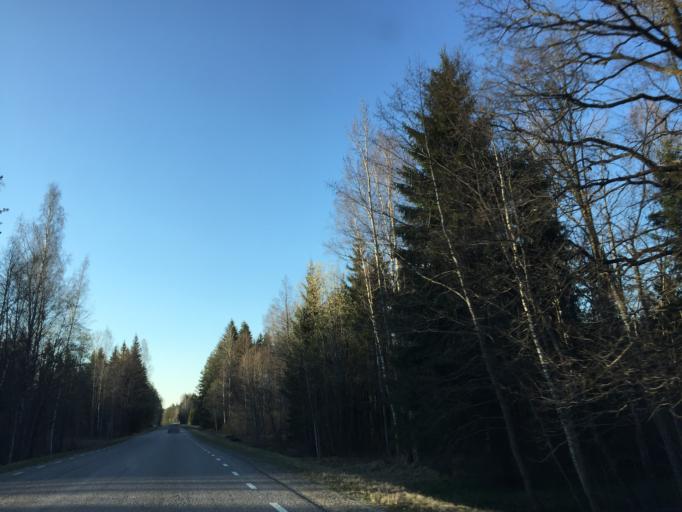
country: EE
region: Ida-Virumaa
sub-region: Toila vald
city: Voka
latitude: 59.1479
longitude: 27.6096
